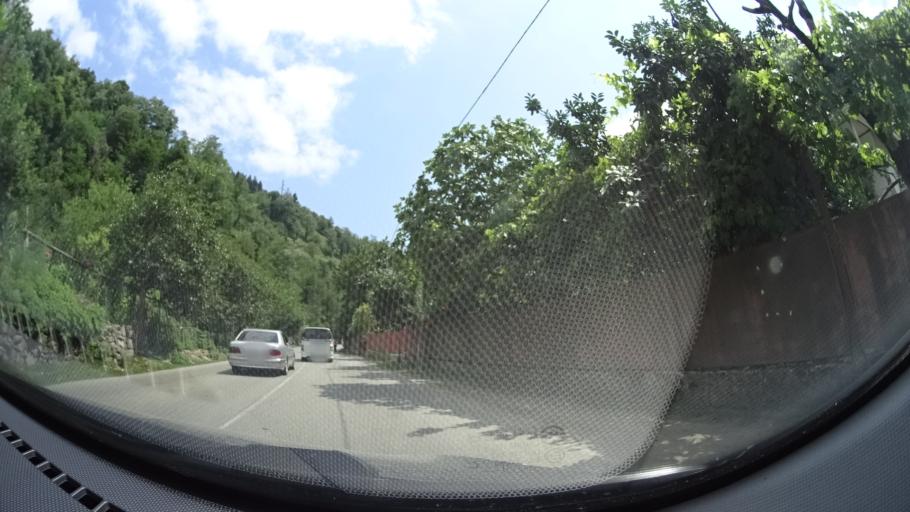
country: GE
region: Ajaria
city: Keda
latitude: 41.5703
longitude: 41.8494
